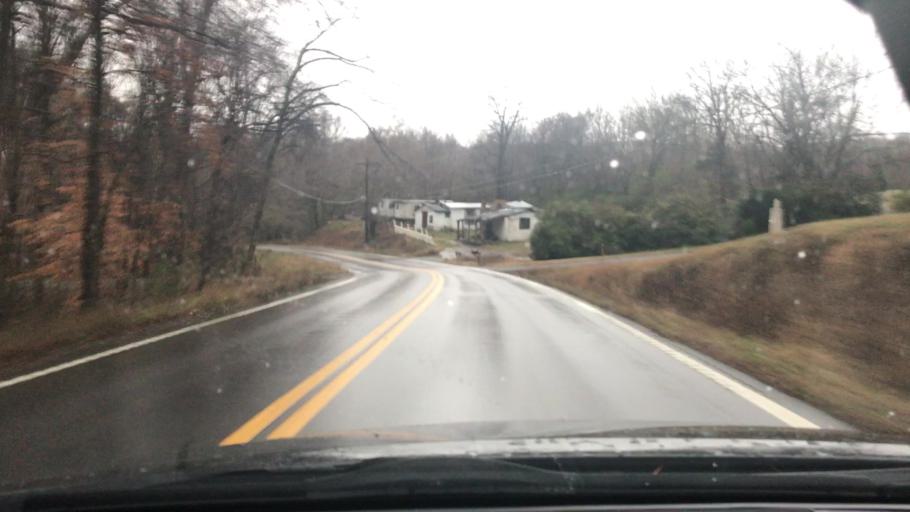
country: US
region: Tennessee
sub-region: Cheatham County
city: Ashland City
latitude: 36.2882
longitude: -87.1628
